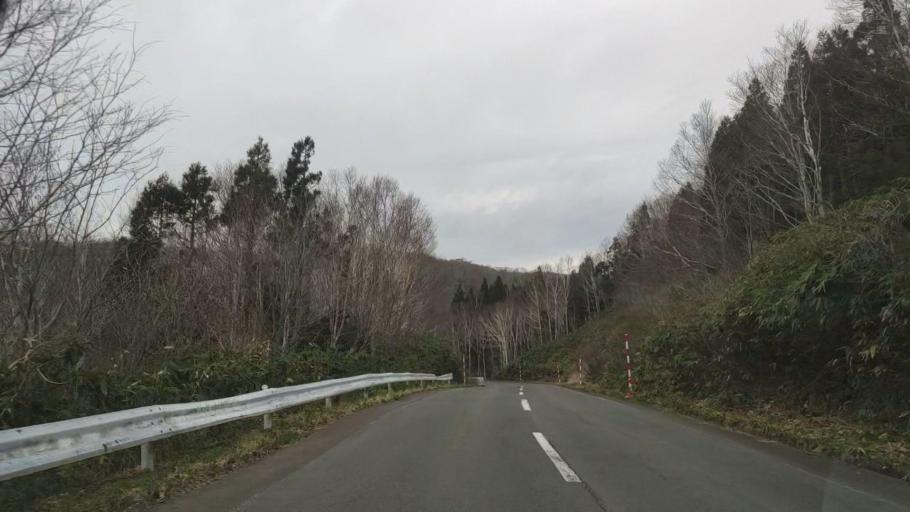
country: JP
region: Akita
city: Hanawa
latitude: 40.4166
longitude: 140.8407
